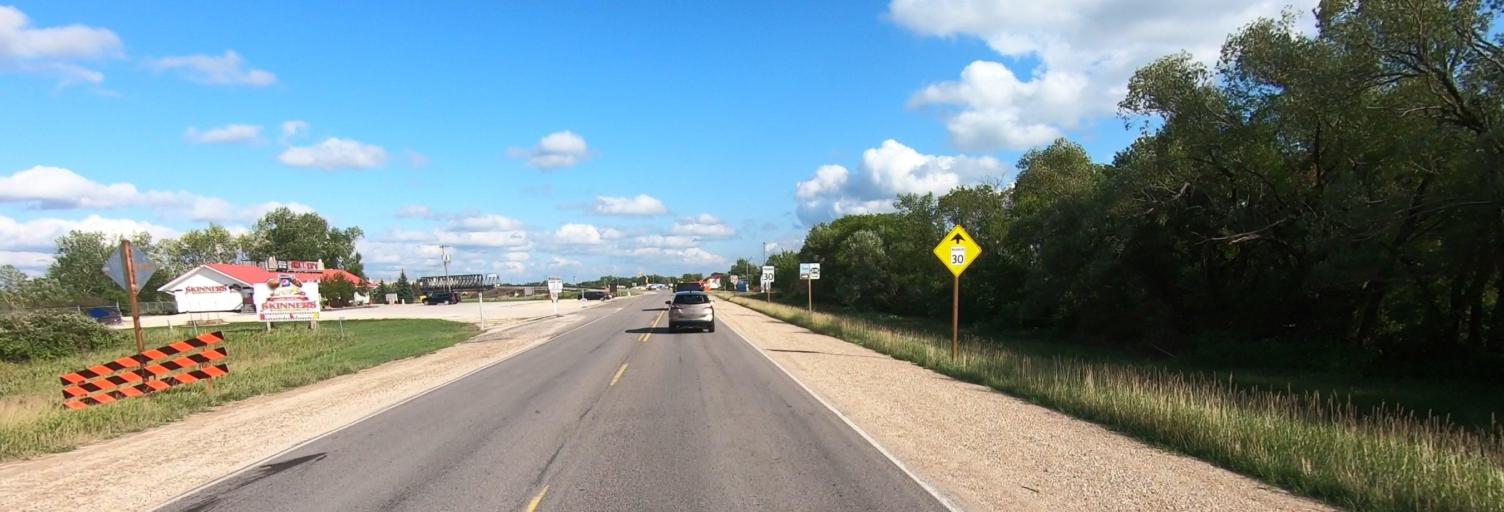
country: CA
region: Manitoba
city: Selkirk
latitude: 50.0856
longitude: -96.9484
